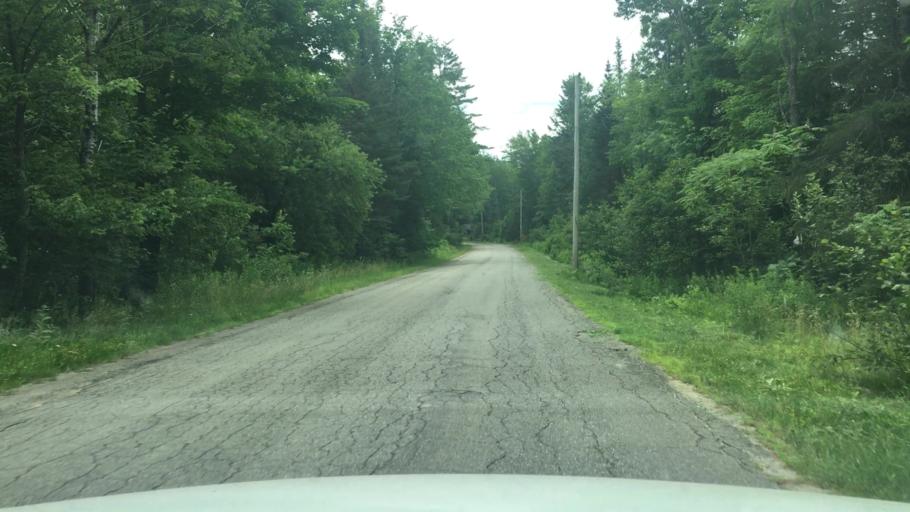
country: US
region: Maine
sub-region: Kennebec County
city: Albion
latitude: 44.4603
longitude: -69.3342
